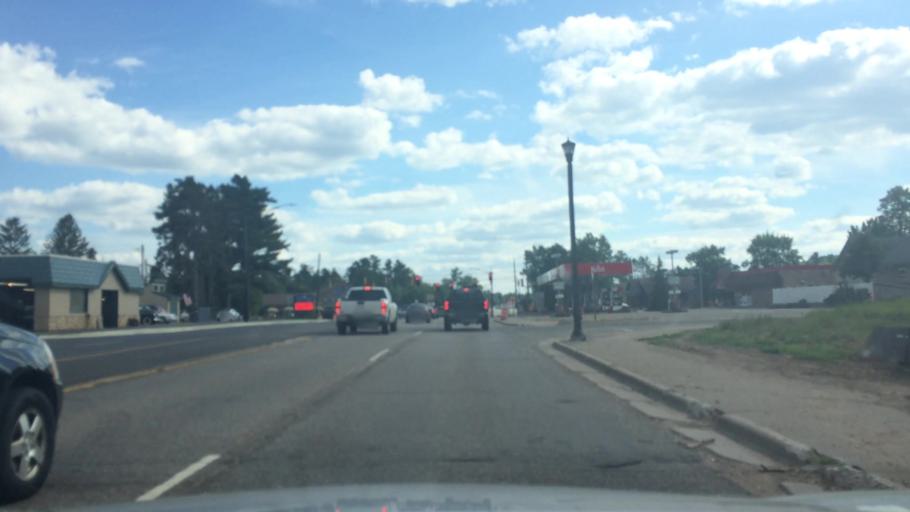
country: US
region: Wisconsin
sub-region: Vilas County
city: Lac du Flambeau
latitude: 45.8959
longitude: -89.6982
